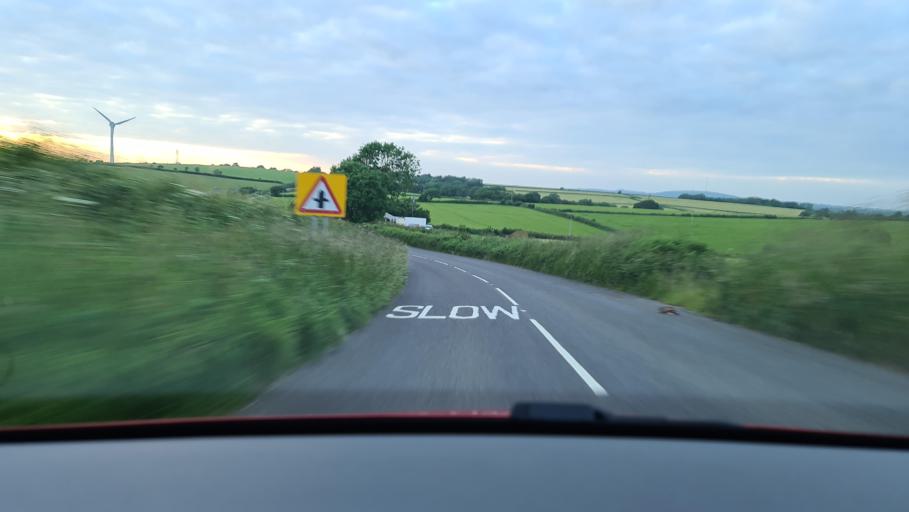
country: GB
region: England
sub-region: Cornwall
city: Liskeard
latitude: 50.4112
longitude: -4.4261
